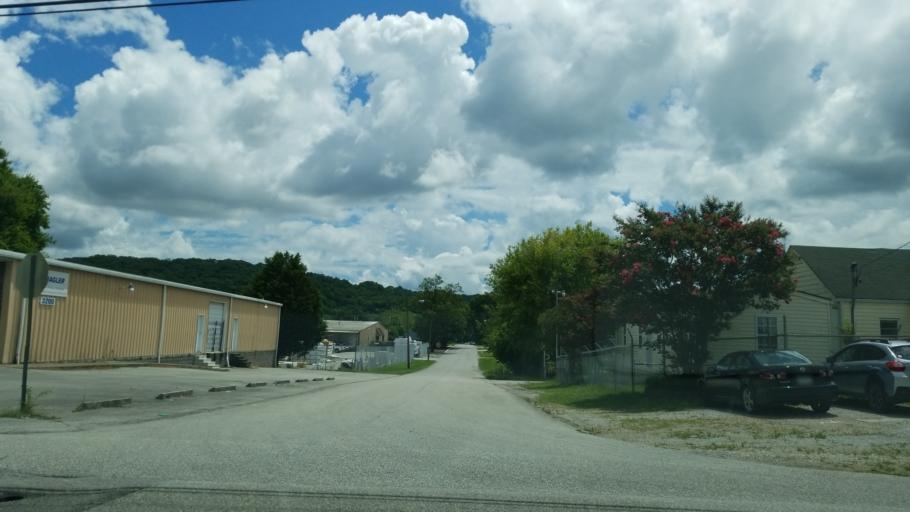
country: US
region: Tennessee
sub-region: Hamilton County
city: East Chattanooga
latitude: 35.0772
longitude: -85.2572
